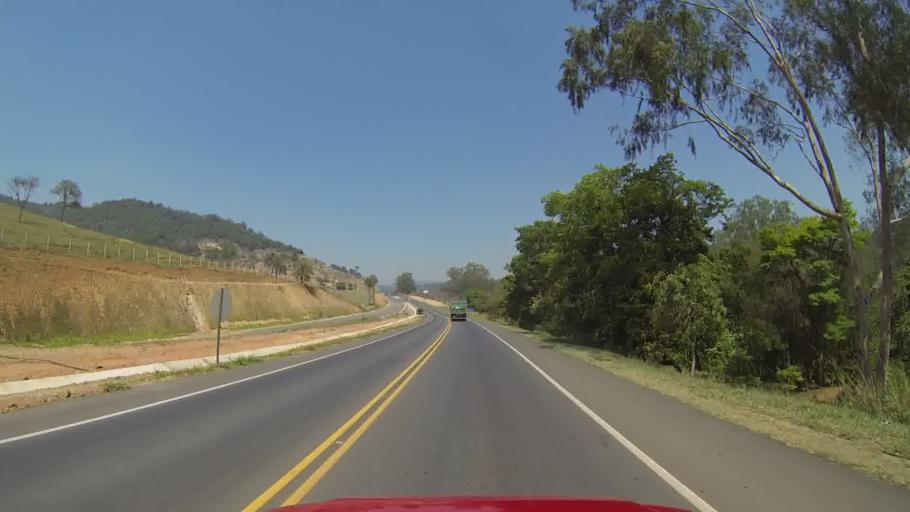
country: BR
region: Minas Gerais
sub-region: Mateus Leme
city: Mateus Leme
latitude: -20.0140
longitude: -44.4854
